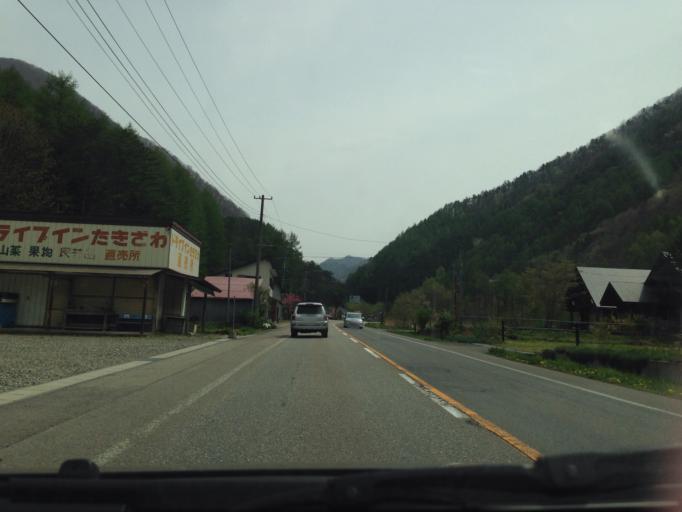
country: JP
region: Tochigi
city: Kuroiso
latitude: 37.1033
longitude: 139.7244
